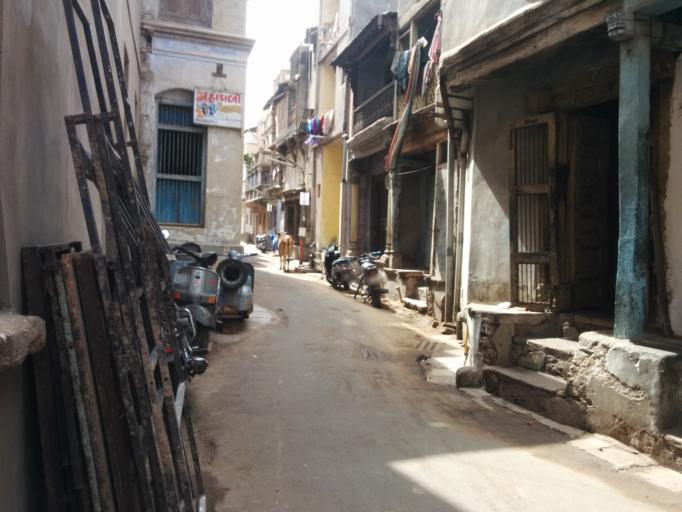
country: IN
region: Gujarat
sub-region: Ahmadabad
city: Ahmedabad
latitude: 23.0187
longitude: 72.5948
